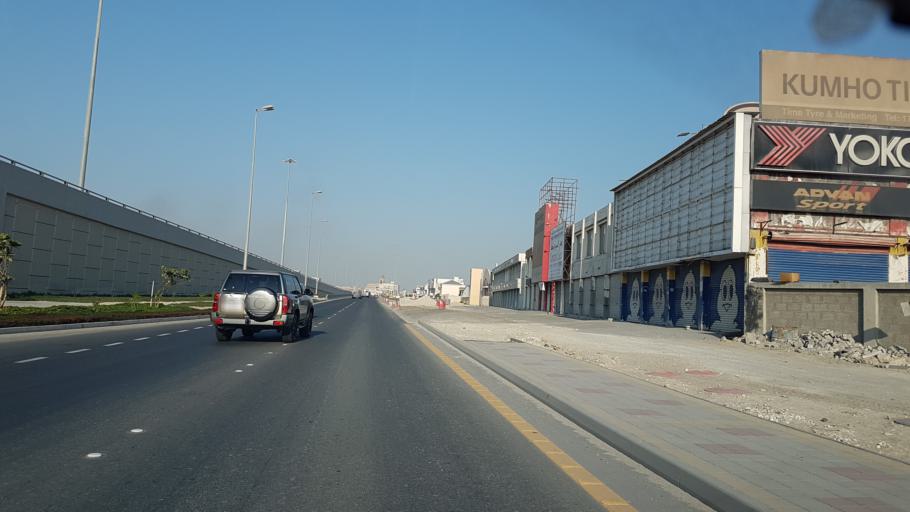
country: BH
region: Northern
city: Sitrah
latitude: 26.1313
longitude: 50.6023
